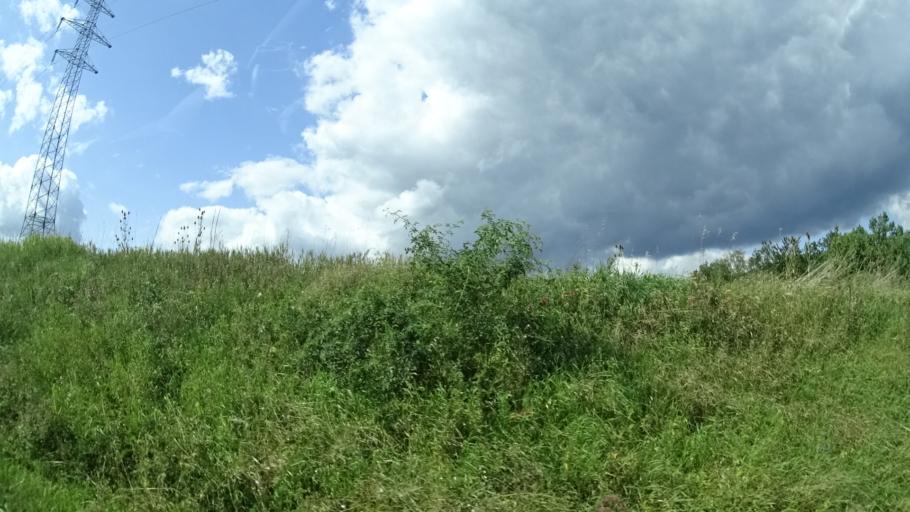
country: DE
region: Bavaria
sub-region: Regierungsbezirk Unterfranken
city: Kirchlauter
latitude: 50.0341
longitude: 10.7582
